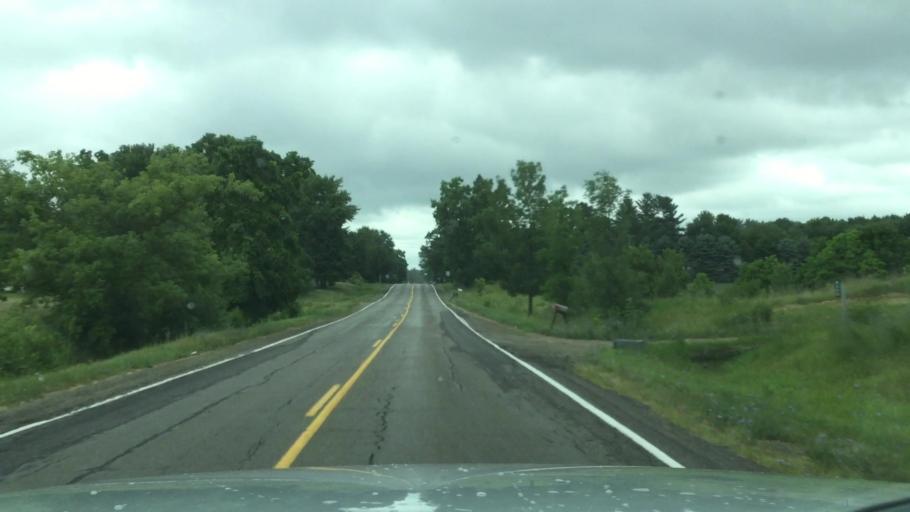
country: US
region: Michigan
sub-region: Genesee County
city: Clio
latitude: 43.1425
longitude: -83.7739
